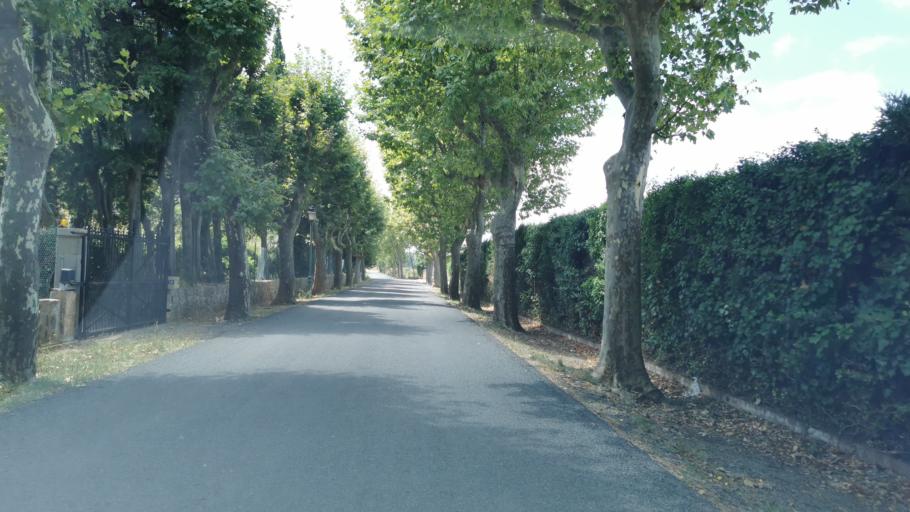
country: FR
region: Languedoc-Roussillon
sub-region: Departement de l'Aude
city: Bizanet
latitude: 43.1612
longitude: 2.8679
